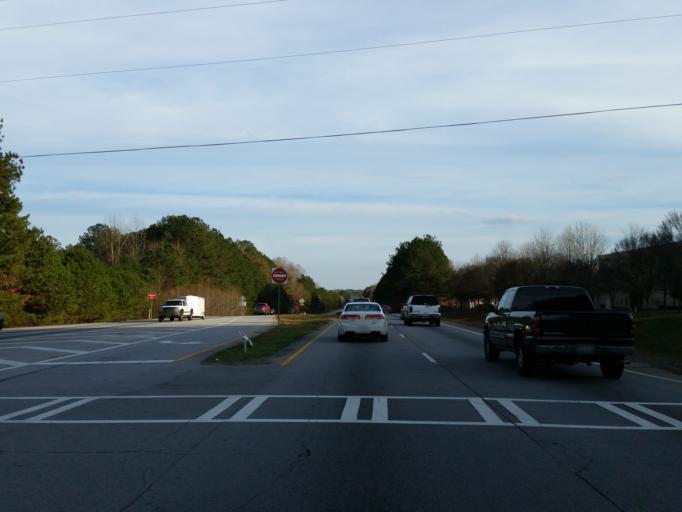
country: US
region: Georgia
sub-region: Cobb County
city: Powder Springs
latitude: 33.8797
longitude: -84.7184
